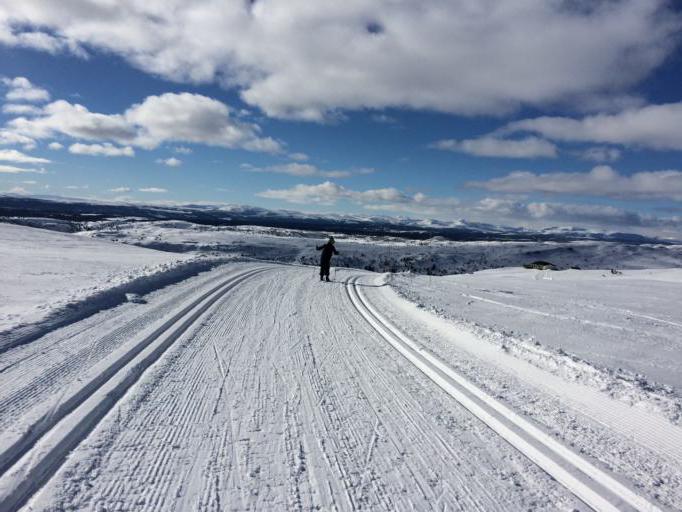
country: NO
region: Oppland
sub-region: Ringebu
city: Ringebu
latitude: 61.3587
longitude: 10.0838
